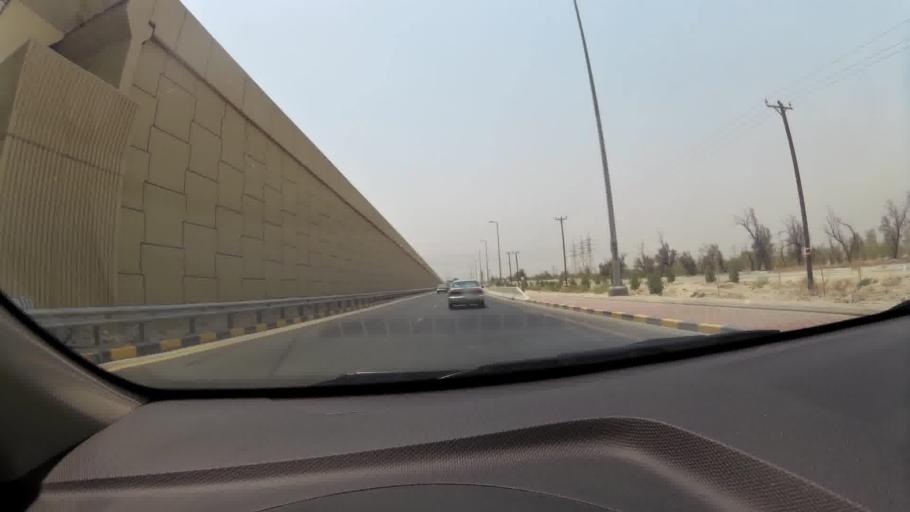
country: KW
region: Al Asimah
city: Ar Rabiyah
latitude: 29.3117
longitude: 47.8044
